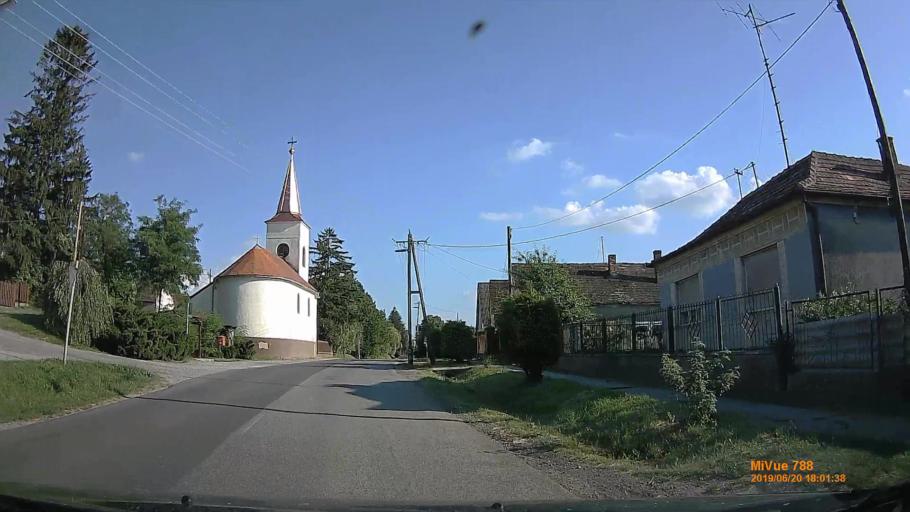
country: HU
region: Baranya
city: Buekkoesd
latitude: 46.0814
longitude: 17.9904
